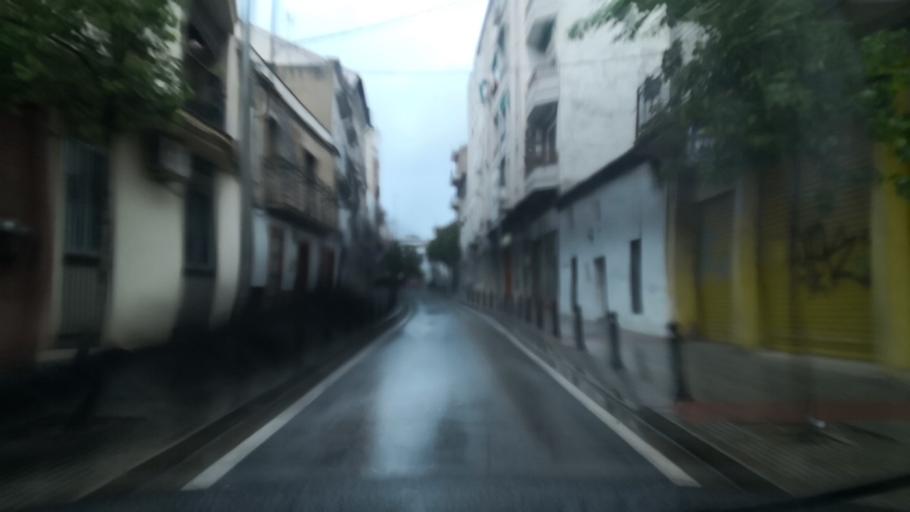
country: ES
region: Extremadura
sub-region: Provincia de Badajoz
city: Merida
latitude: 38.9181
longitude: -6.3490
